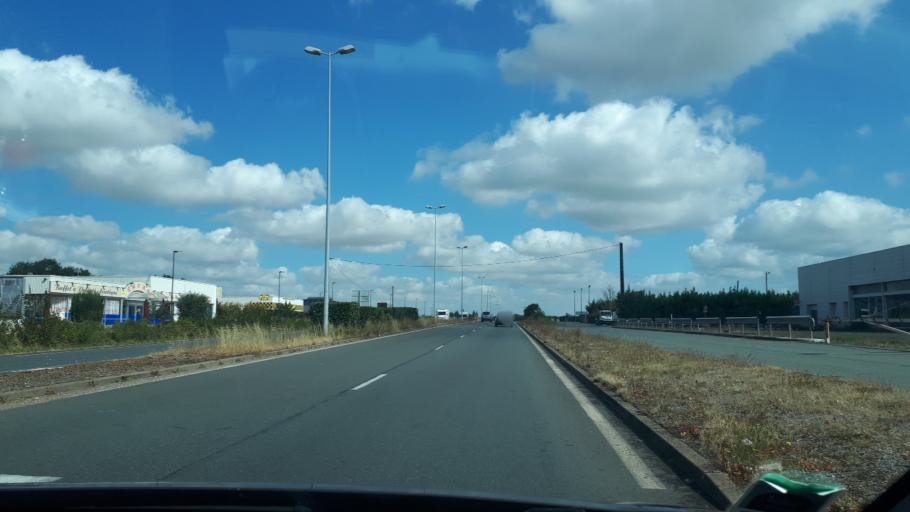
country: FR
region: Centre
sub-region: Departement du Loir-et-Cher
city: Saint-Ouen
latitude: 47.8186
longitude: 1.0761
